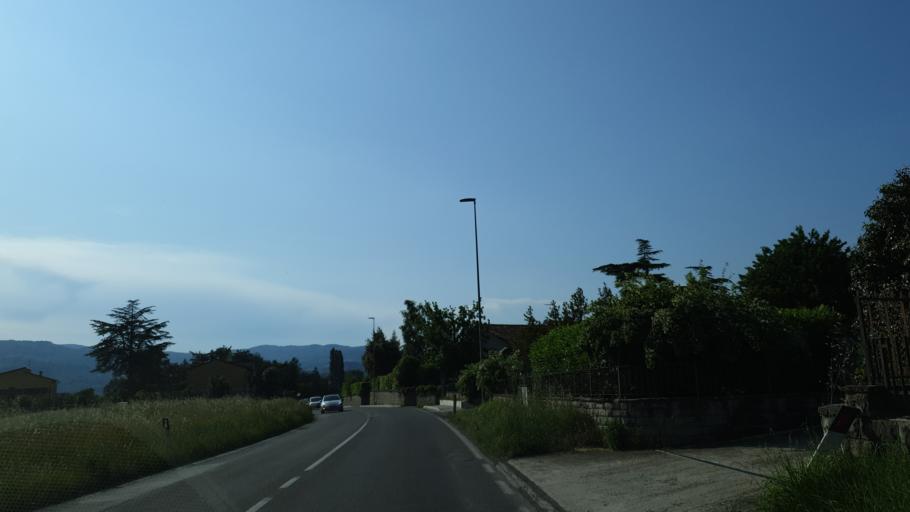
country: IT
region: Tuscany
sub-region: Province of Arezzo
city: Ponte a Poppi
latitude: 43.7355
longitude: 11.7563
